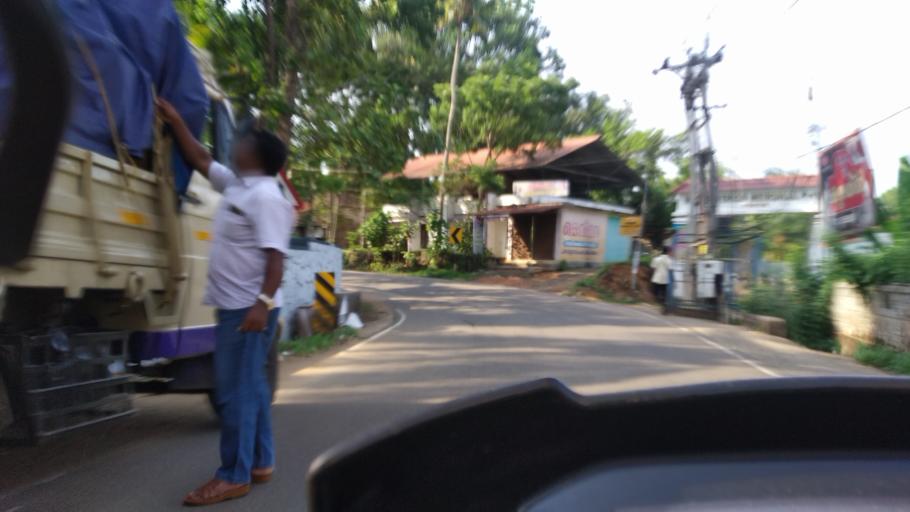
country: IN
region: Kerala
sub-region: Ernakulam
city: Piravam
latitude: 9.8738
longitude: 76.4957
